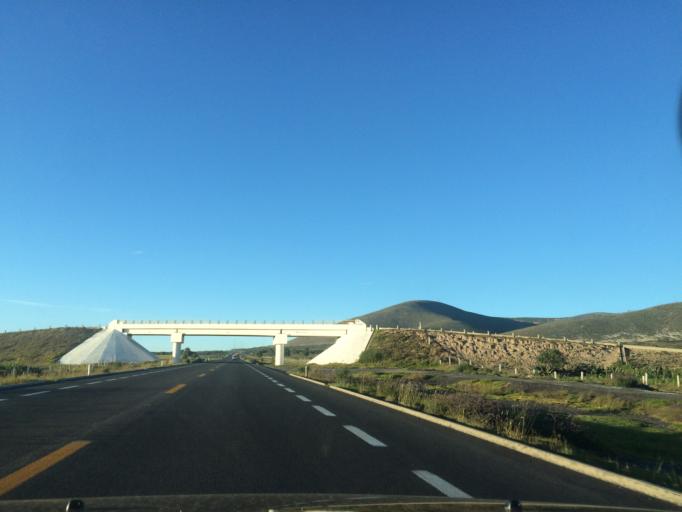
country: MX
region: Puebla
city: Morelos Canada
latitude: 18.7419
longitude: -97.4778
